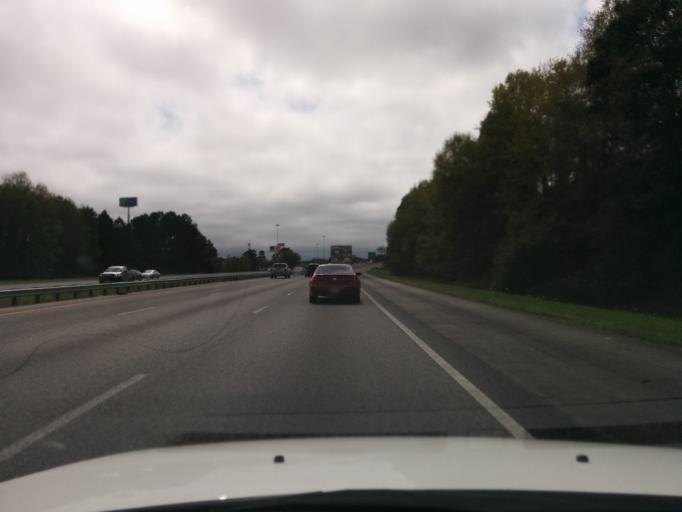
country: US
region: Georgia
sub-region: Chatham County
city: Georgetown
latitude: 32.0104
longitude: -81.2786
